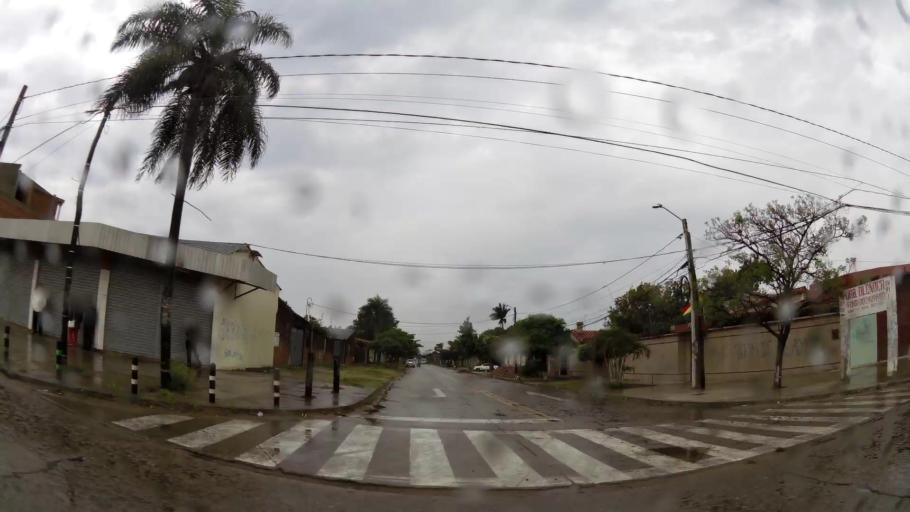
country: BO
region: Santa Cruz
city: Santa Cruz de la Sierra
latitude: -17.8101
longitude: -63.1490
